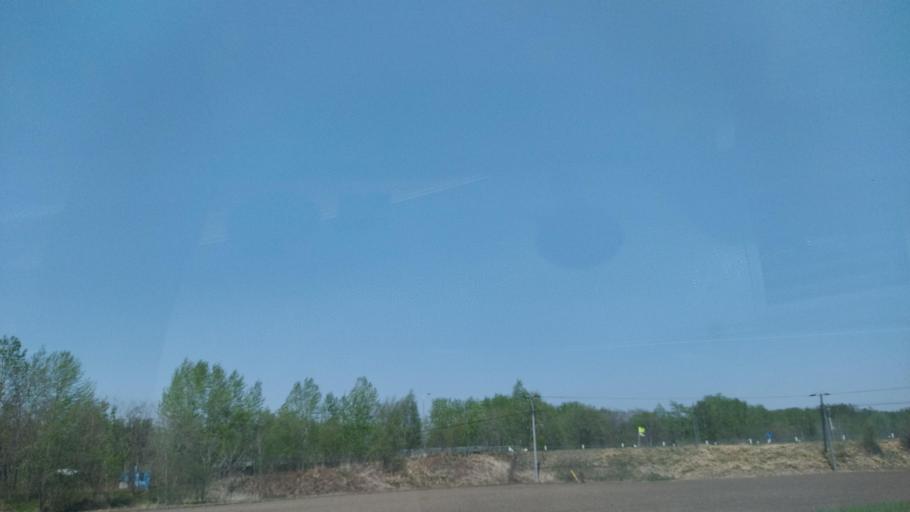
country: JP
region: Hokkaido
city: Obihiro
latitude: 42.9015
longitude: 143.0109
